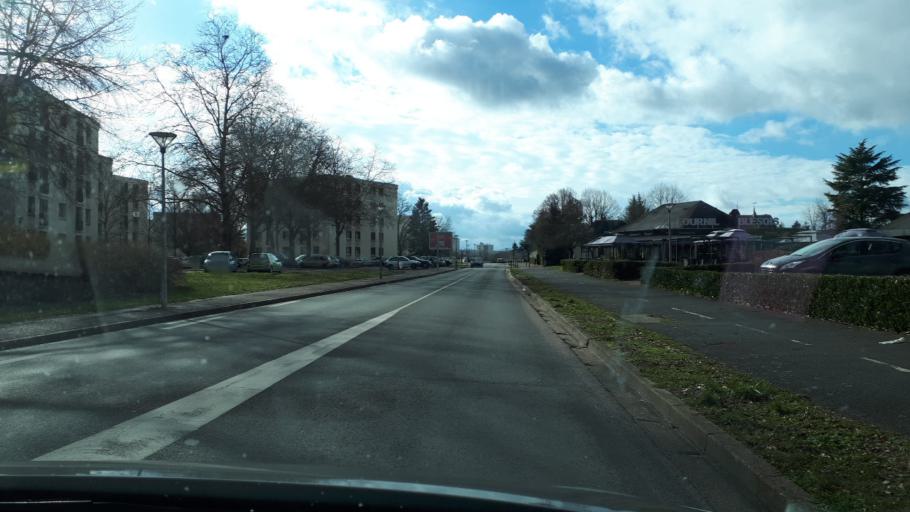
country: FR
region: Centre
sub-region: Departement du Loir-et-Cher
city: Villebarou
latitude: 47.5990
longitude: 1.3085
